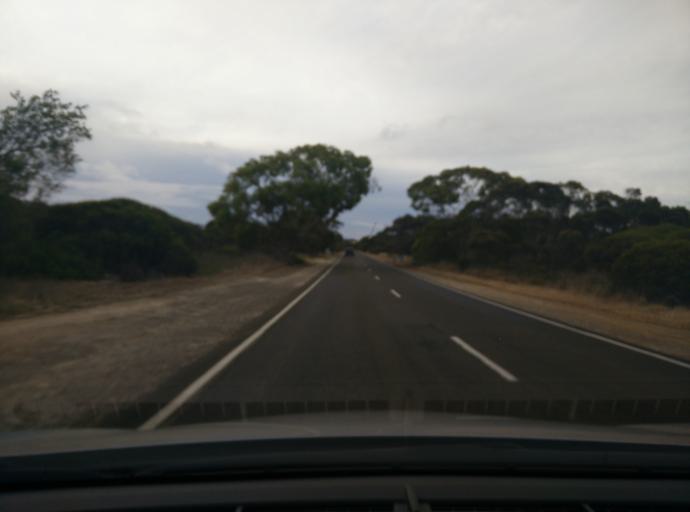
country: AU
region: South Australia
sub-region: Kangaroo Island
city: Kingscote
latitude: -35.8062
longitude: 137.6742
